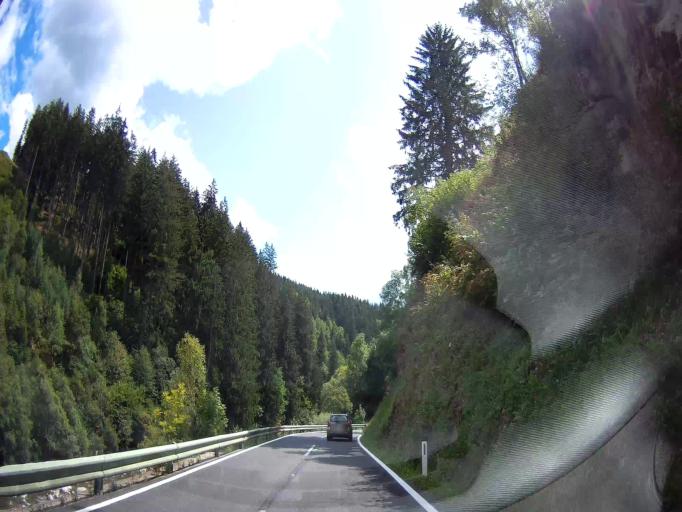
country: AT
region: Carinthia
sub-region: Politischer Bezirk Spittal an der Drau
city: Trebesing
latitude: 46.8666
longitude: 13.5065
